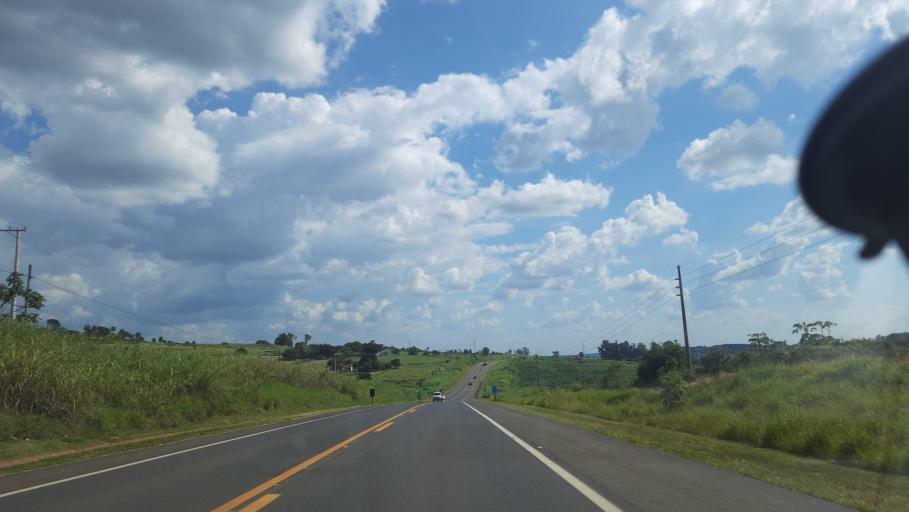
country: BR
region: Sao Paulo
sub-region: Sao Jose Do Rio Pardo
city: Sao Jose do Rio Pardo
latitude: -21.6768
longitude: -46.9252
